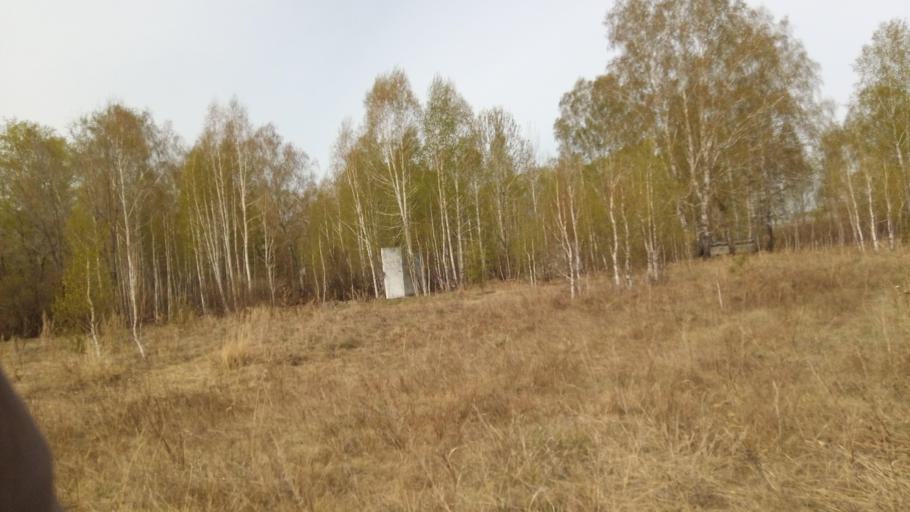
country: RU
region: Chelyabinsk
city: Timiryazevskiy
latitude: 55.0258
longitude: 60.8592
